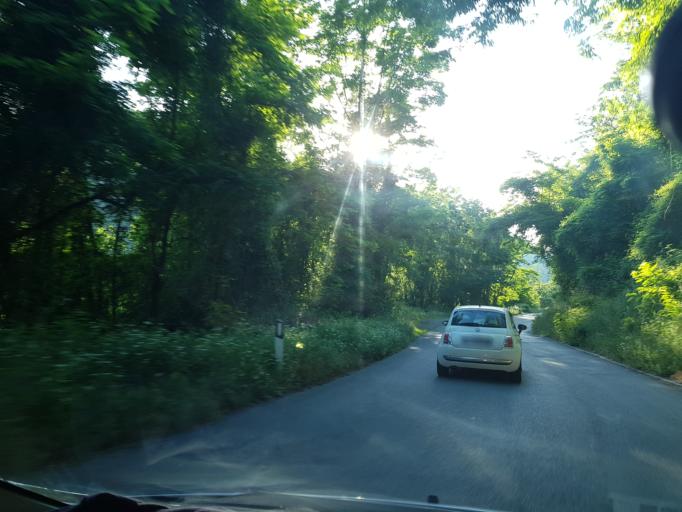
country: IT
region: Tuscany
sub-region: Provincia di Lucca
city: Minucciano
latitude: 44.1856
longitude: 10.1950
